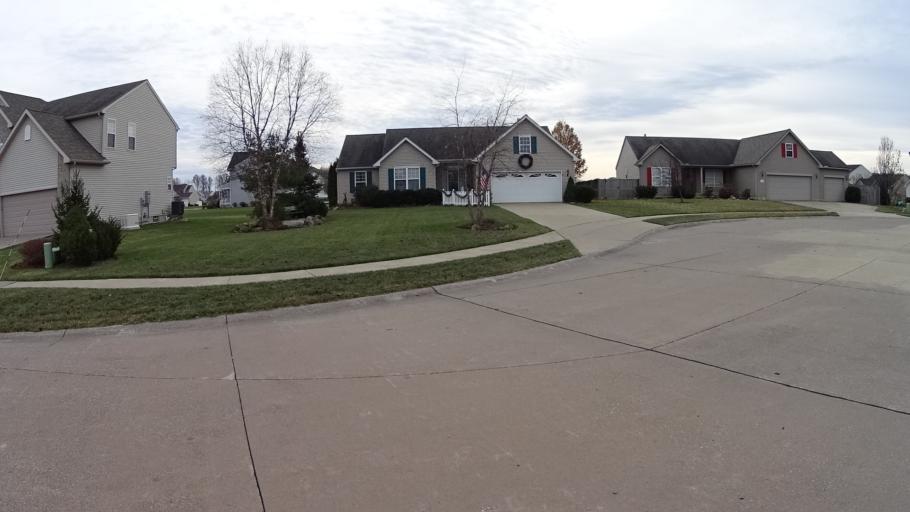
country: US
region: Ohio
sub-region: Lorain County
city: North Ridgeville
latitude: 41.4031
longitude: -82.0396
